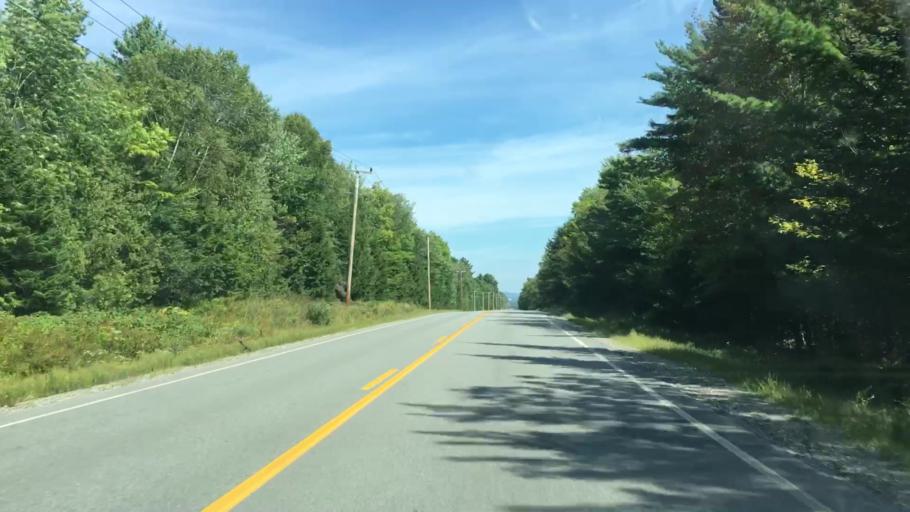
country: US
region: Maine
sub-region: Penobscot County
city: Howland
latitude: 45.2308
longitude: -68.7694
